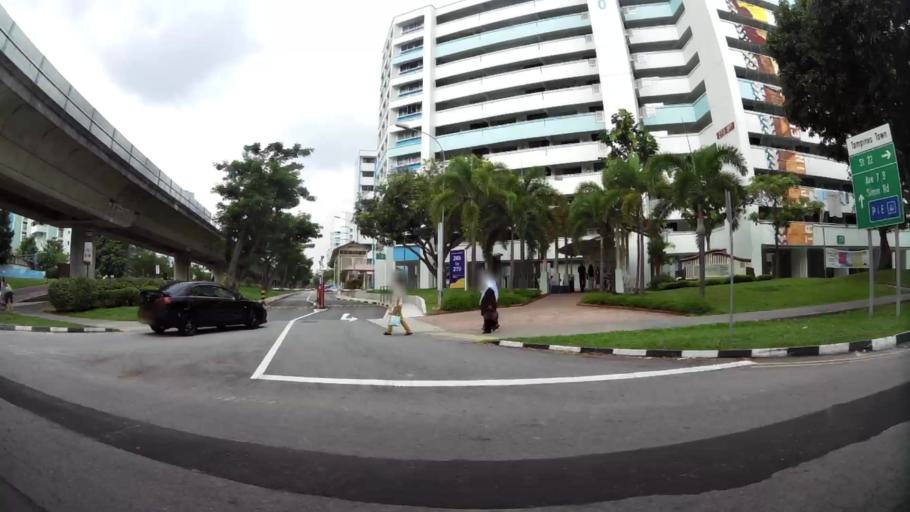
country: SG
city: Singapore
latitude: 1.3493
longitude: 103.9487
